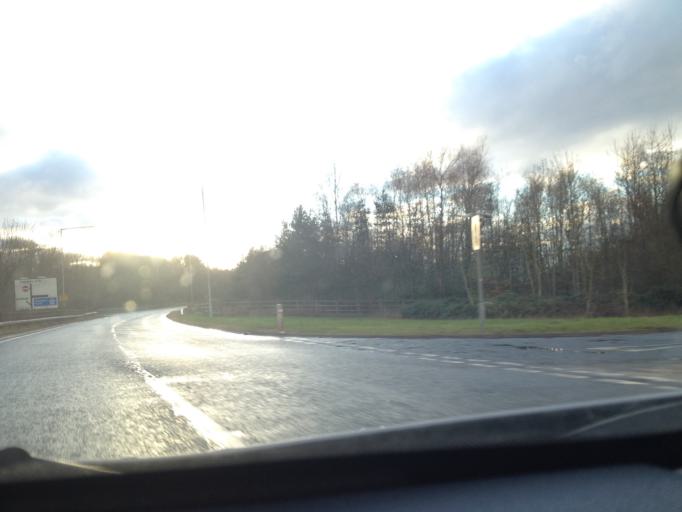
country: GB
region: Scotland
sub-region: South Lanarkshire
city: Larkhall
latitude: 55.7532
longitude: -3.9669
